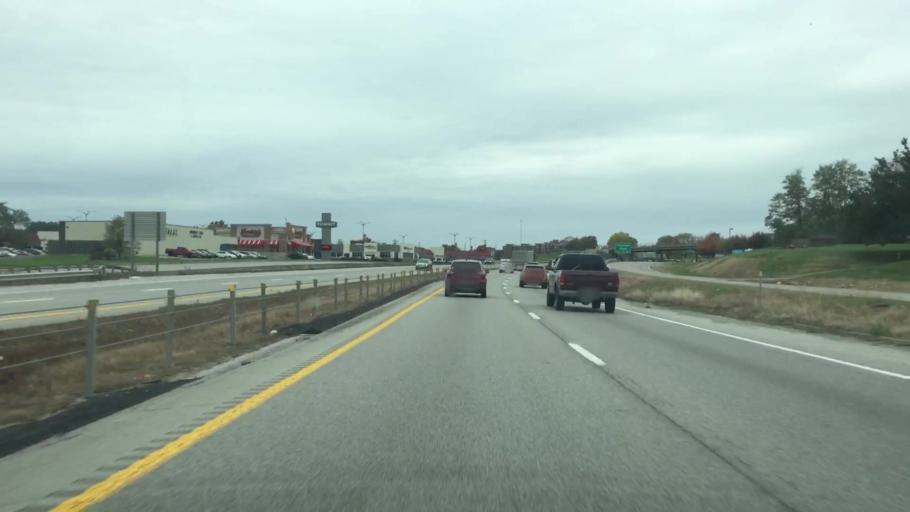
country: US
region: Missouri
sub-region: Jackson County
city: Lees Summit
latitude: 38.9156
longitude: -94.3990
